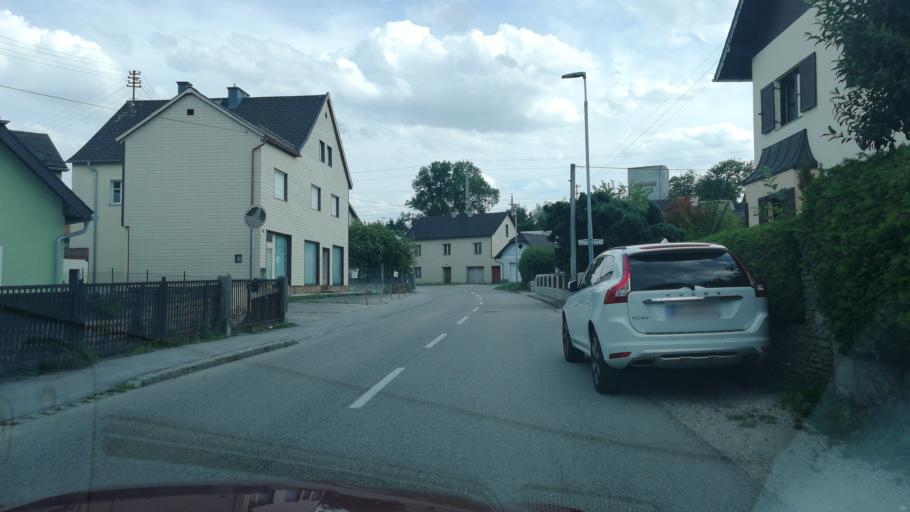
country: AT
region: Upper Austria
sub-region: Wels-Land
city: Lambach
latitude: 48.0955
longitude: 13.8685
